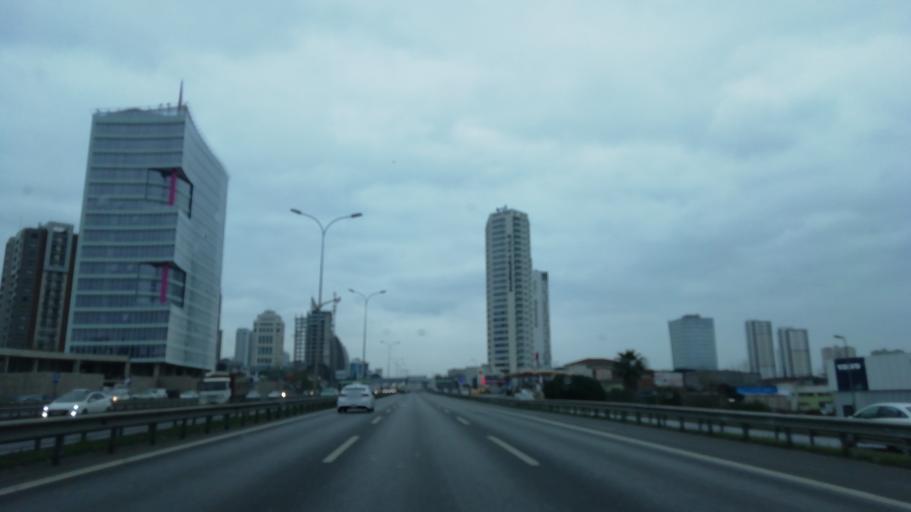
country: TR
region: Istanbul
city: Maltepe
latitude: 40.9121
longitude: 29.1930
